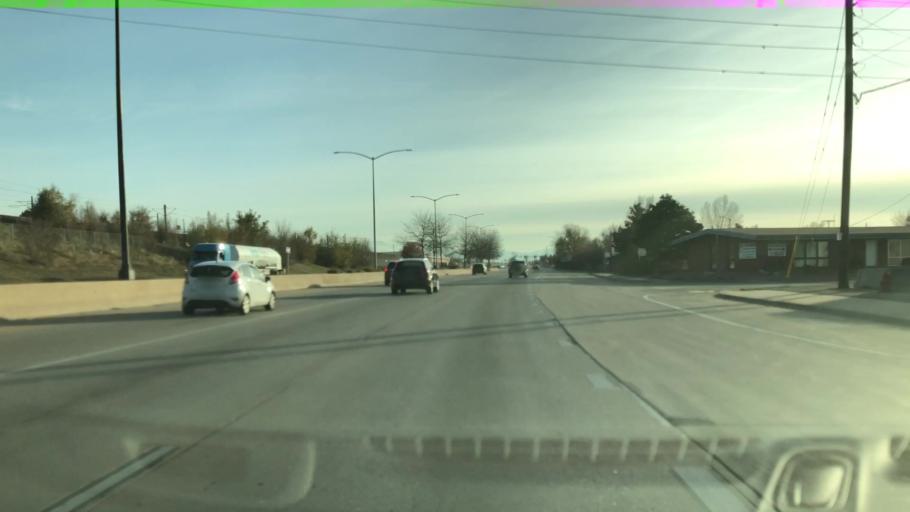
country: US
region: Colorado
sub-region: Arapahoe County
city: Englewood
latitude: 39.6644
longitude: -104.9971
